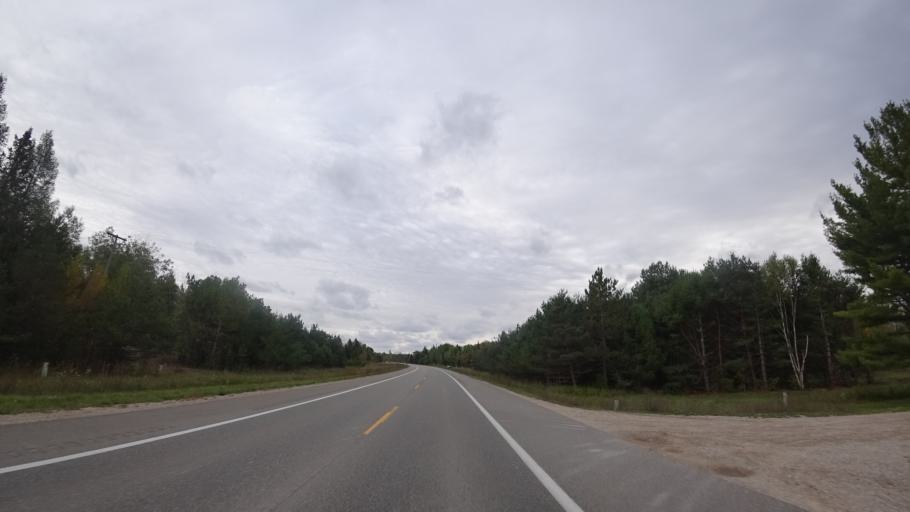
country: US
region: Michigan
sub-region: Charlevoix County
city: Boyne City
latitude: 45.1517
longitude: -84.9178
